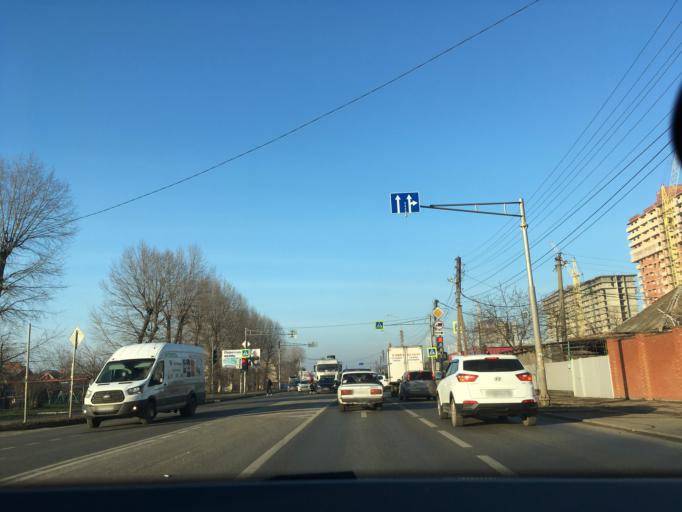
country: RU
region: Krasnodarskiy
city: Krasnodar
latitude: 45.1039
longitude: 39.0129
